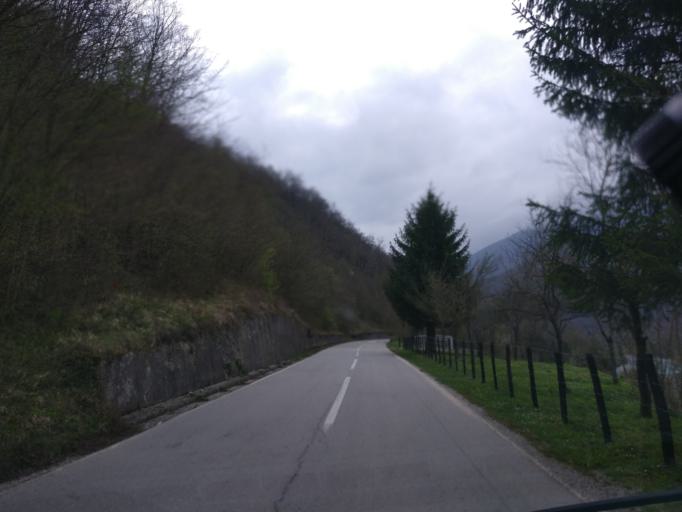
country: BA
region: Republika Srpska
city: Foca
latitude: 43.4651
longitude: 18.7474
